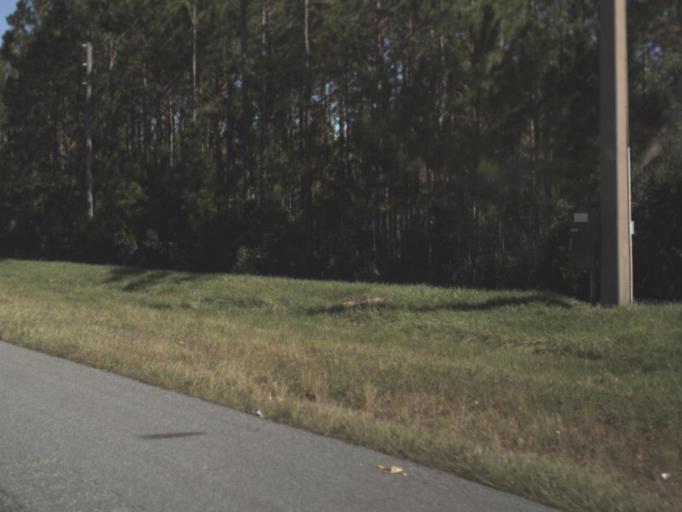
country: US
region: Florida
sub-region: Pasco County
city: Odessa
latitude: 28.2103
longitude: -82.5482
